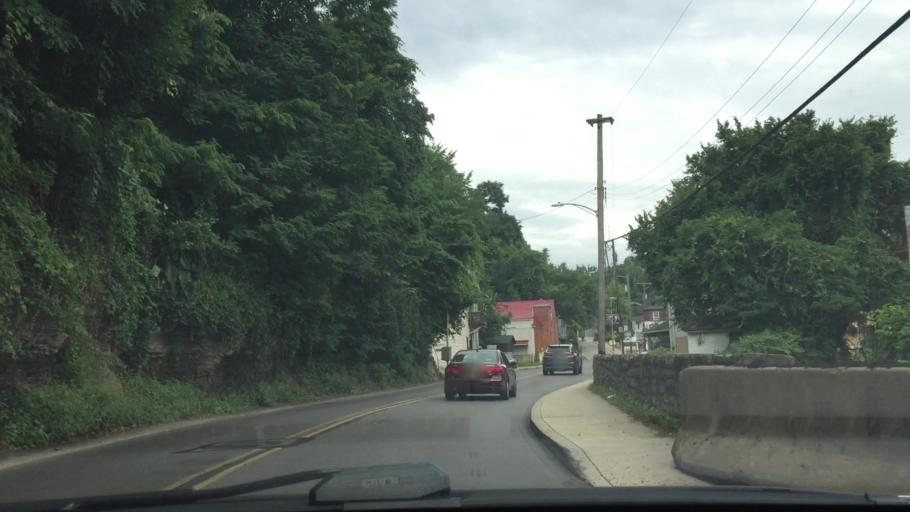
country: US
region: Pennsylvania
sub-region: Allegheny County
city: Bridgeville
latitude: 40.3584
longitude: -80.1070
